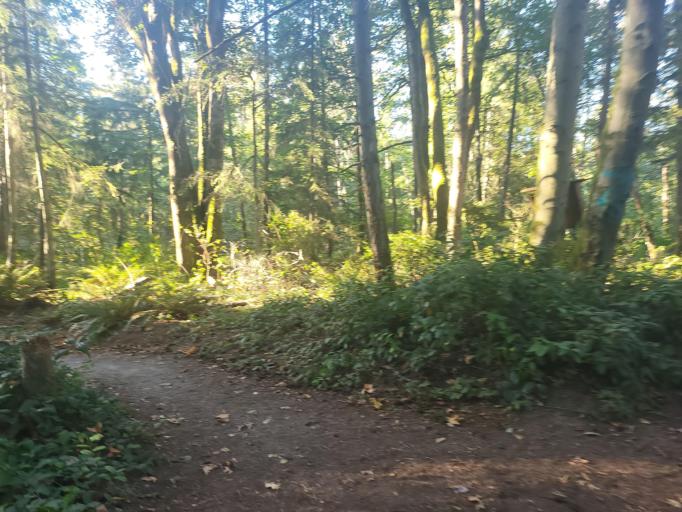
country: US
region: Washington
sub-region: Pierce County
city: Tacoma
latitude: 47.3143
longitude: -122.4083
